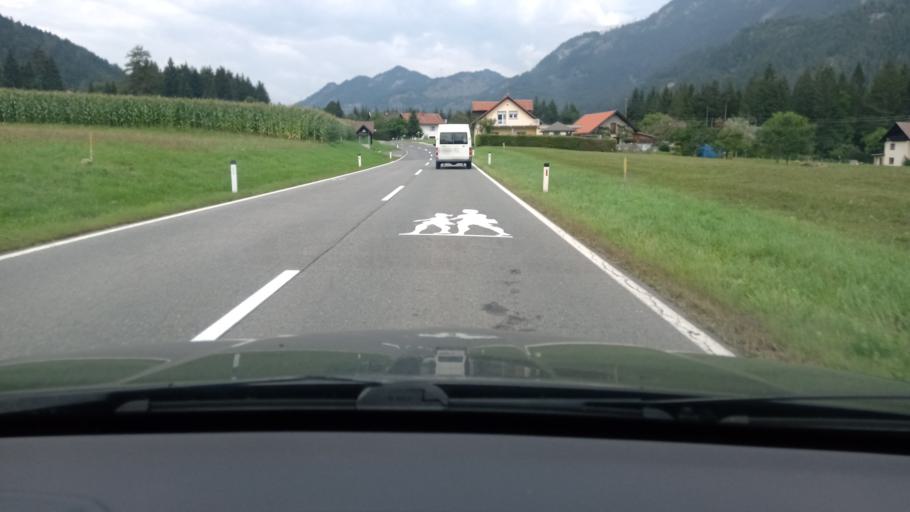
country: AT
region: Carinthia
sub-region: Politischer Bezirk Hermagor
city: Hermagor
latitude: 46.6441
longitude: 13.3378
